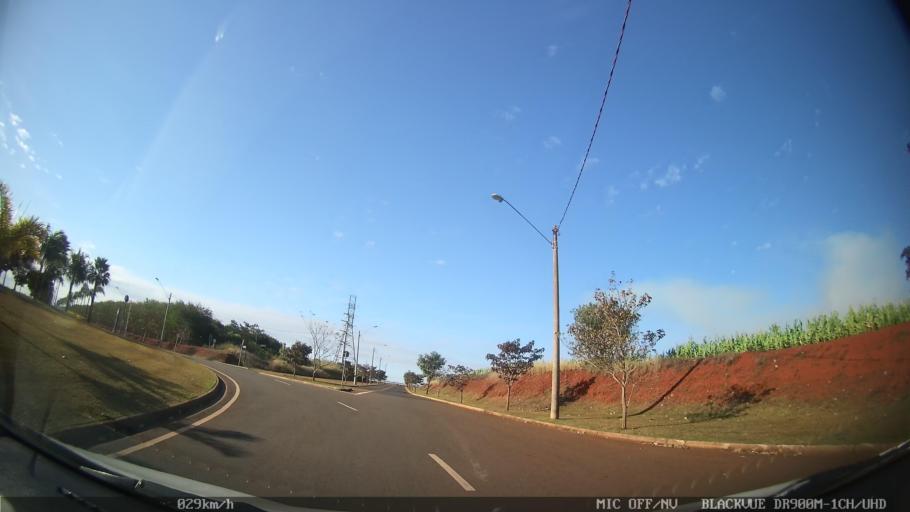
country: BR
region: Sao Paulo
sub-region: Piracicaba
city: Piracicaba
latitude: -22.6909
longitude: -47.6133
